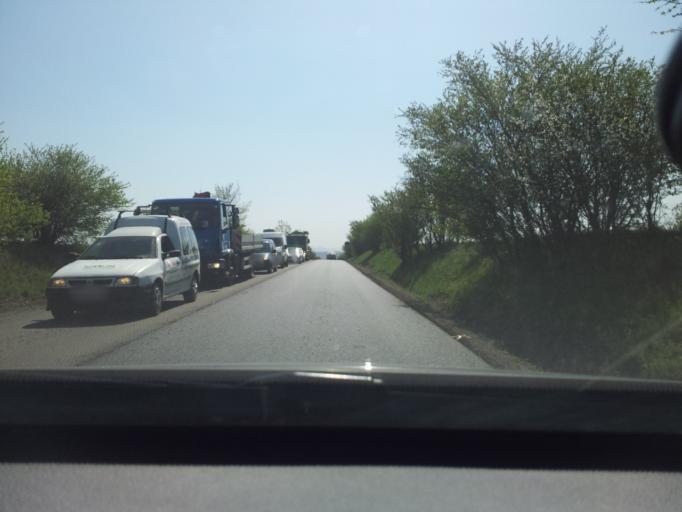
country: SK
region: Nitriansky
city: Banovce nad Bebravou
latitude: 48.7646
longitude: 18.1899
